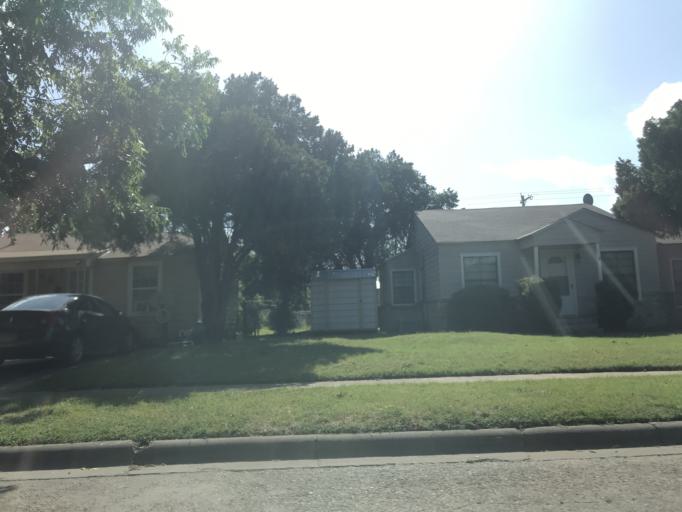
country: US
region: Texas
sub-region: Taylor County
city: Abilene
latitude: 32.4304
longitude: -99.7624
